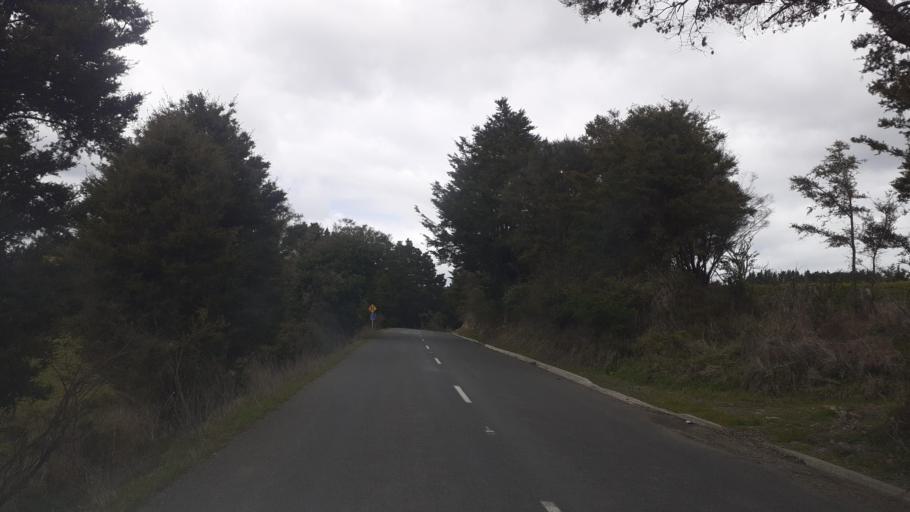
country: NZ
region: Northland
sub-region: Far North District
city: Moerewa
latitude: -35.5837
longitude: 173.9739
